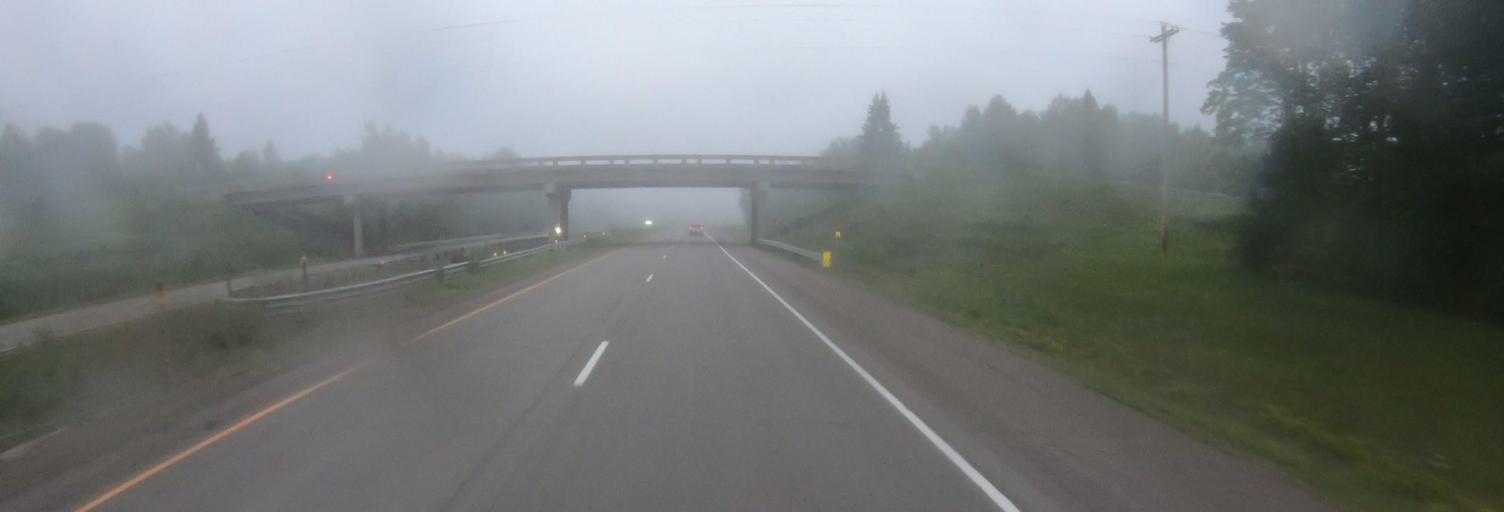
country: US
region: Minnesota
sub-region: Carlton County
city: Carlton
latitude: 46.5766
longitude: -92.5854
